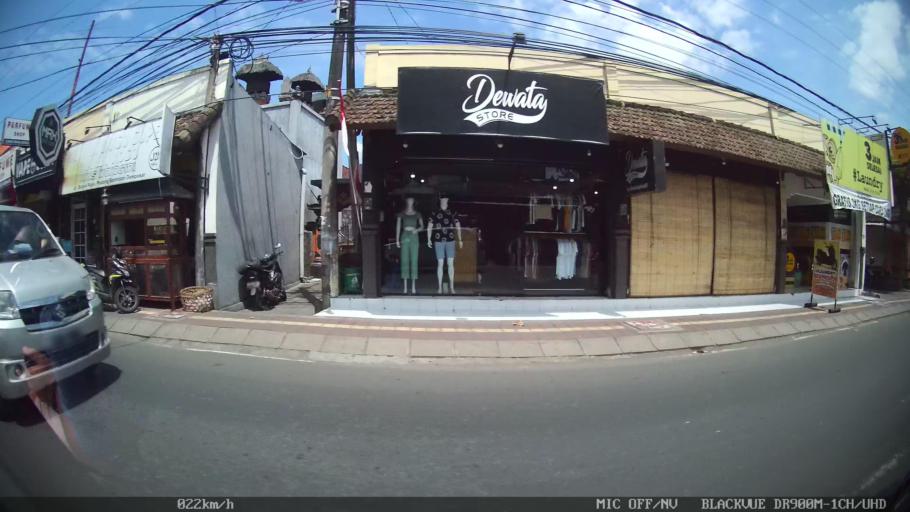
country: ID
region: Bali
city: Denpasar
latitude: -8.6583
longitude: 115.1865
